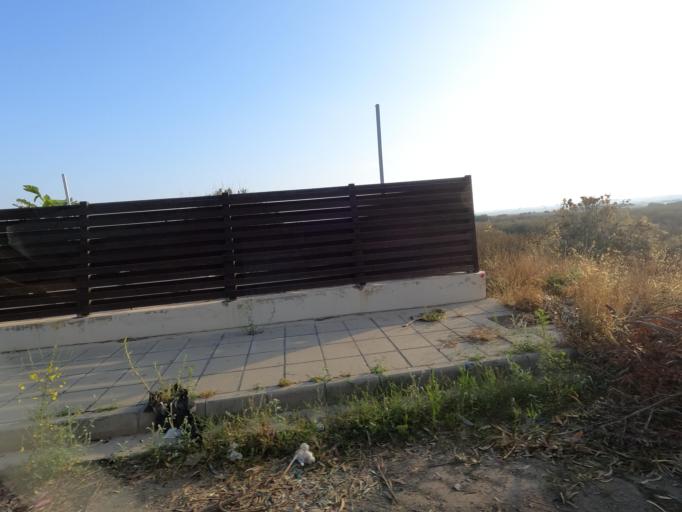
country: CY
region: Ammochostos
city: Paralimni
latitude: 35.0271
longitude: 33.9637
